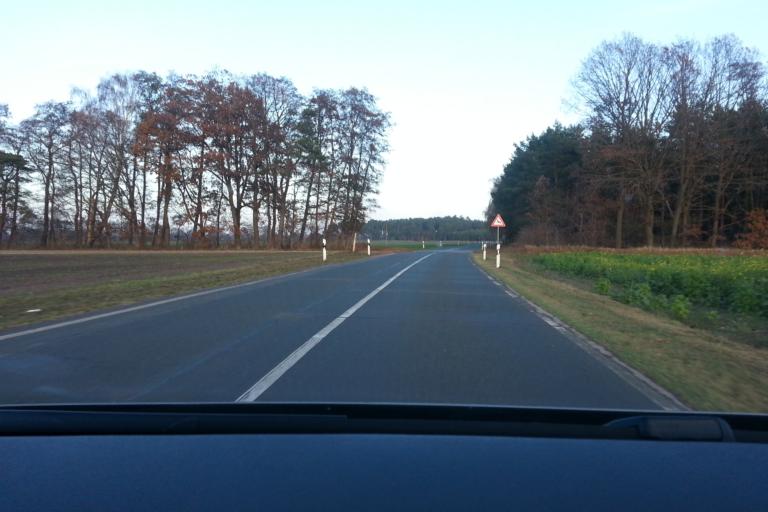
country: DE
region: Mecklenburg-Vorpommern
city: Ferdinandshof
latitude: 53.6281
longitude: 13.7993
